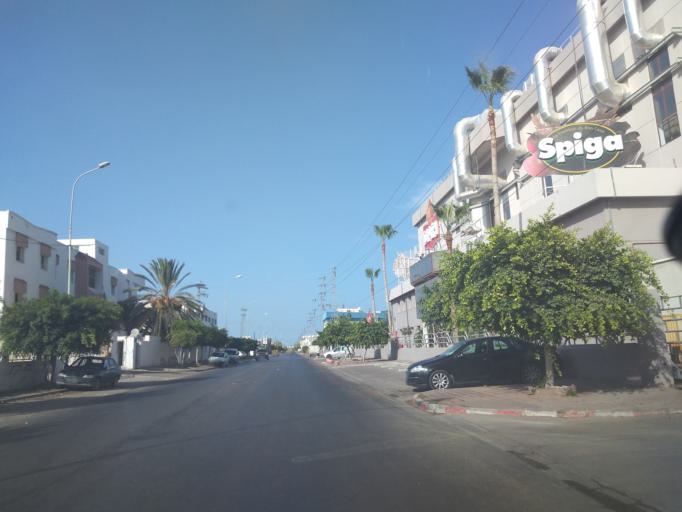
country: TN
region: Safaqis
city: Sfax
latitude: 34.7469
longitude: 10.7709
